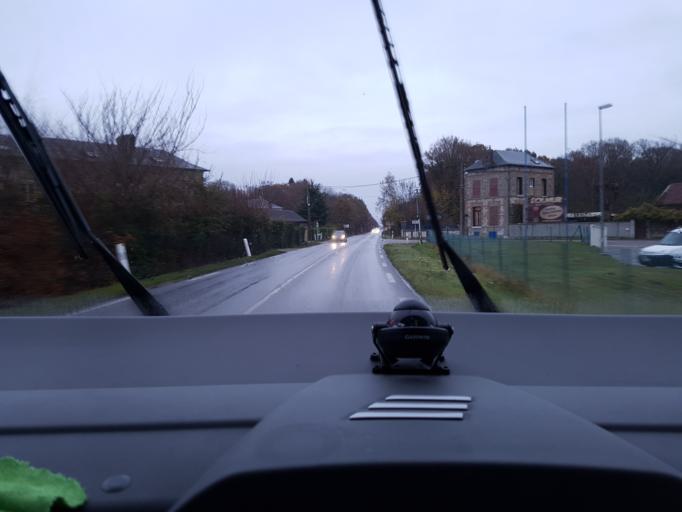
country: FR
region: Haute-Normandie
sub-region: Departement de l'Eure
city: La Saussaye
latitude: 49.2689
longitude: 0.9851
